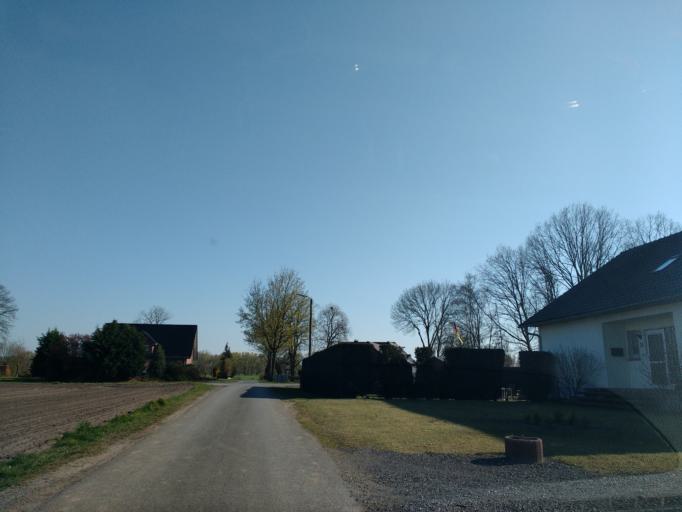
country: DE
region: North Rhine-Westphalia
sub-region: Regierungsbezirk Detmold
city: Delbruck
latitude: 51.7247
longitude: 8.5508
